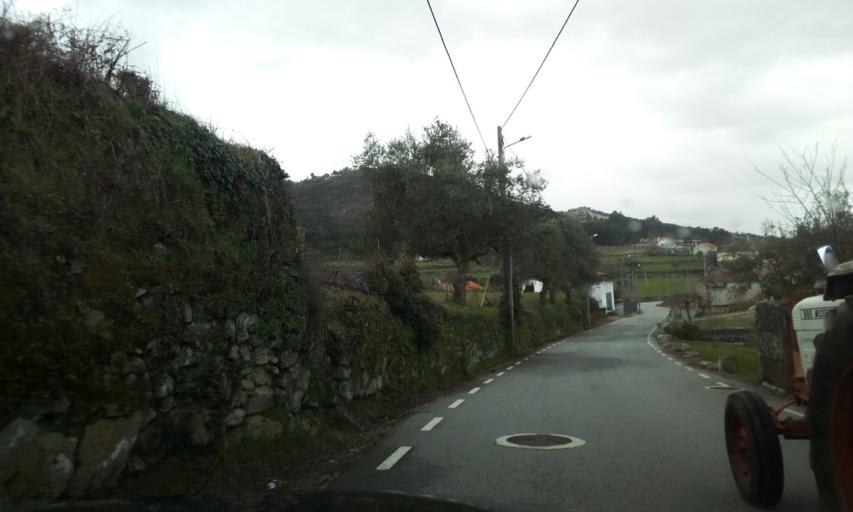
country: PT
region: Guarda
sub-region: Fornos de Algodres
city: Fornos de Algodres
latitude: 40.6395
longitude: -7.5947
